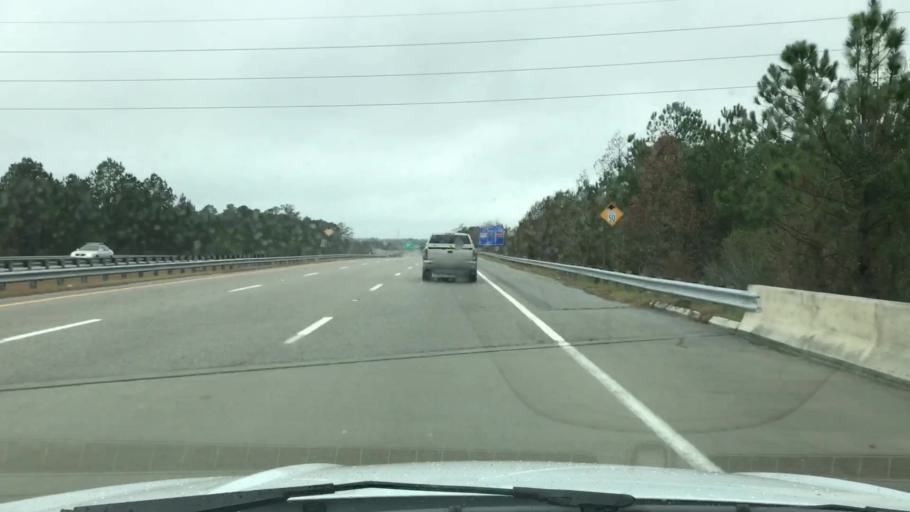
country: US
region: South Carolina
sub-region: Horry County
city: Forestbrook
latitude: 33.7425
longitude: -78.9368
